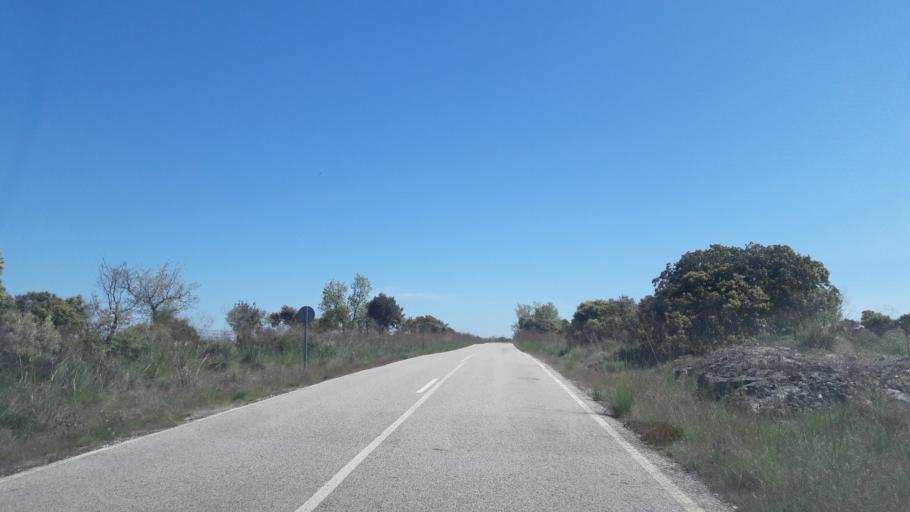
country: ES
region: Castille and Leon
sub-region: Provincia de Salamanca
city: Villarmuerto
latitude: 41.0424
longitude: -6.3906
